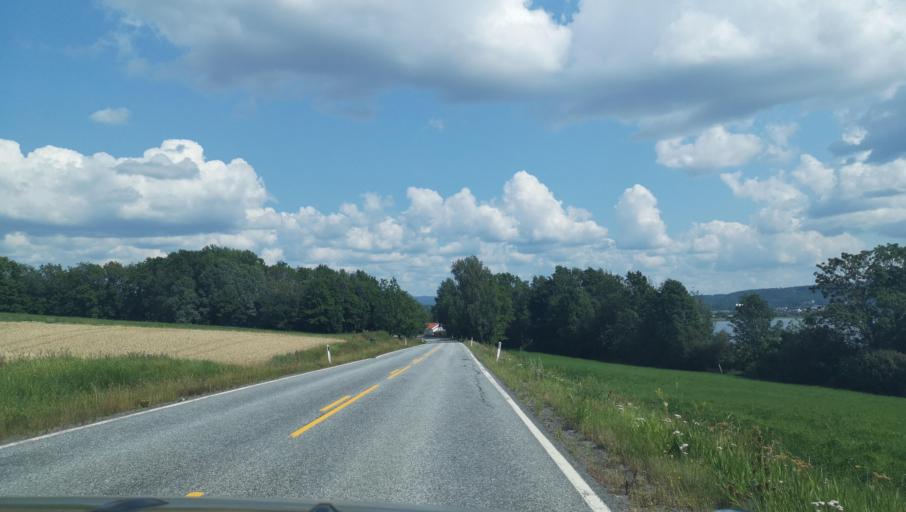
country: NO
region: Buskerud
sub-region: Ovre Eiker
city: Hokksund
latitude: 59.7078
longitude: 9.8138
